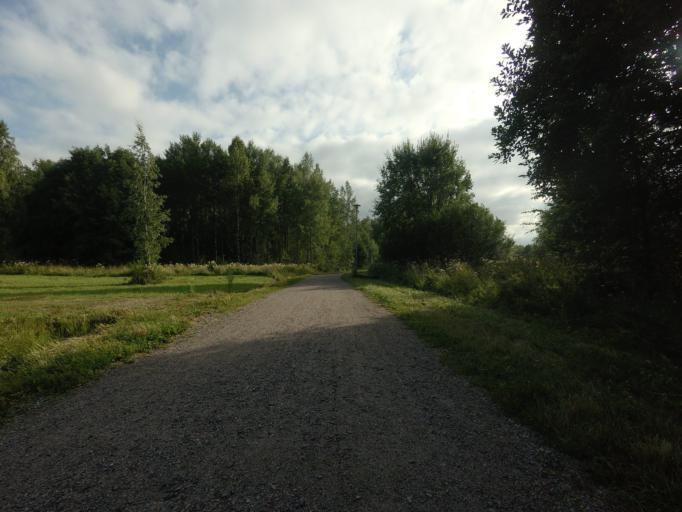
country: FI
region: Uusimaa
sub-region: Helsinki
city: Espoo
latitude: 60.1732
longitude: 24.6754
